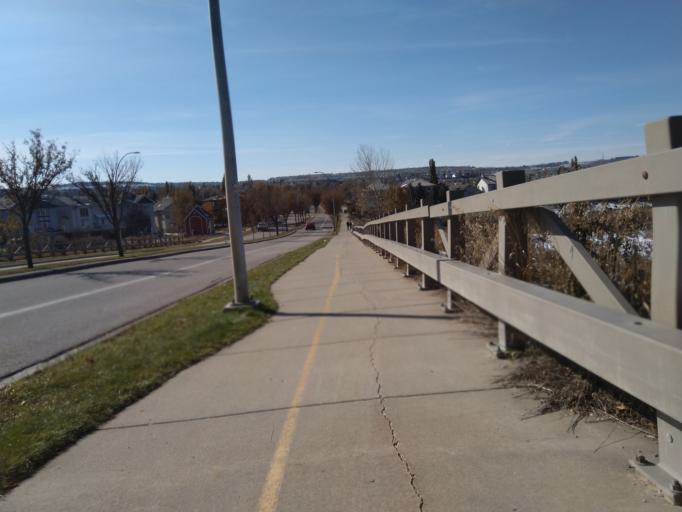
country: CA
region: Alberta
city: Calgary
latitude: 51.1559
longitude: -114.1019
